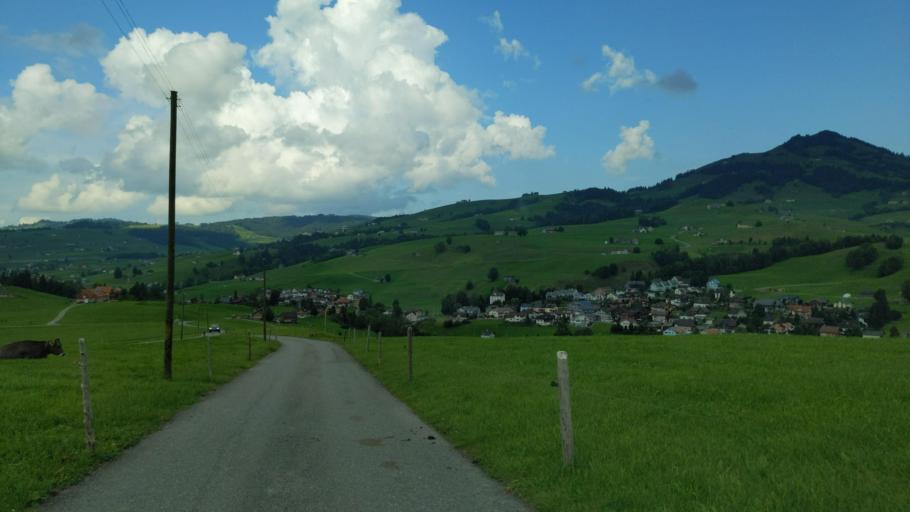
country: CH
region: Appenzell Innerrhoden
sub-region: Appenzell Inner Rhodes
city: Appenzell
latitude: 47.3018
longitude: 9.4283
